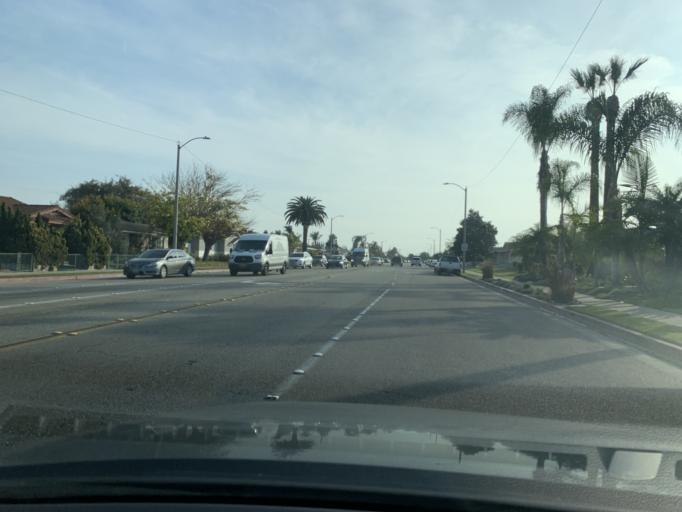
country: US
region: California
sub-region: Orange County
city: Westminster
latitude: 33.7684
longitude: -118.0257
